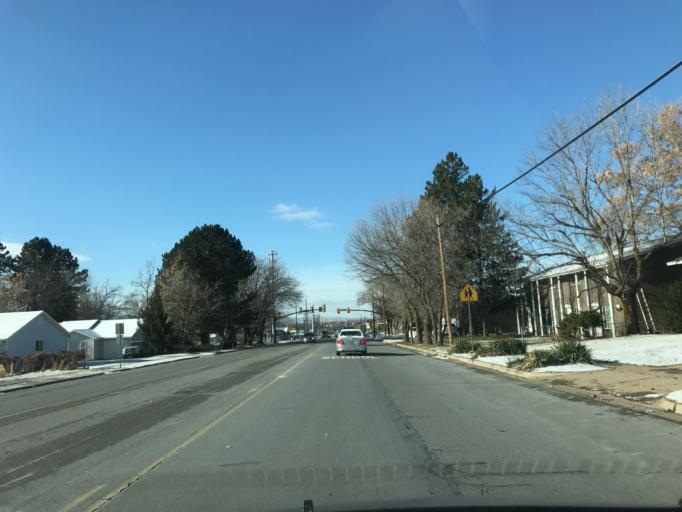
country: US
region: Utah
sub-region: Davis County
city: Kaysville
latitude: 41.0381
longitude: -111.9342
